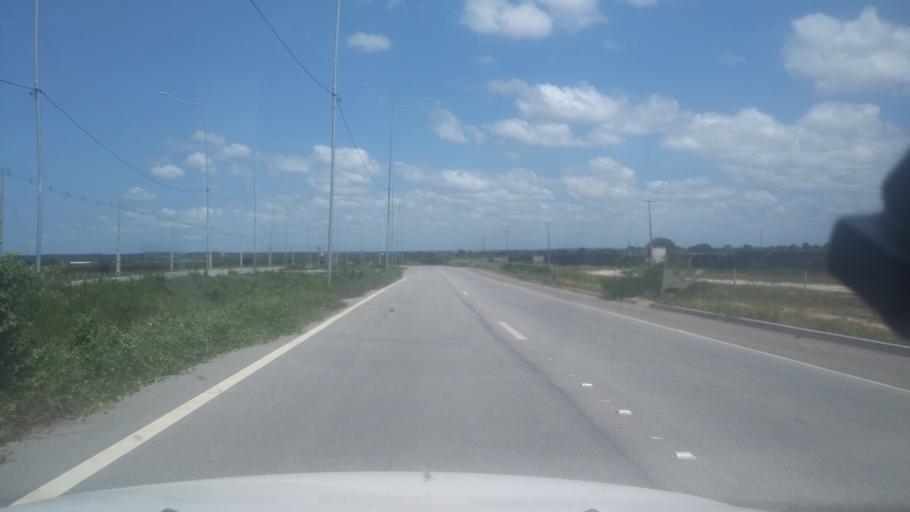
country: BR
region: Rio Grande do Norte
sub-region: Macaiba
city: Macaiba
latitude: -5.8538
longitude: -35.3791
